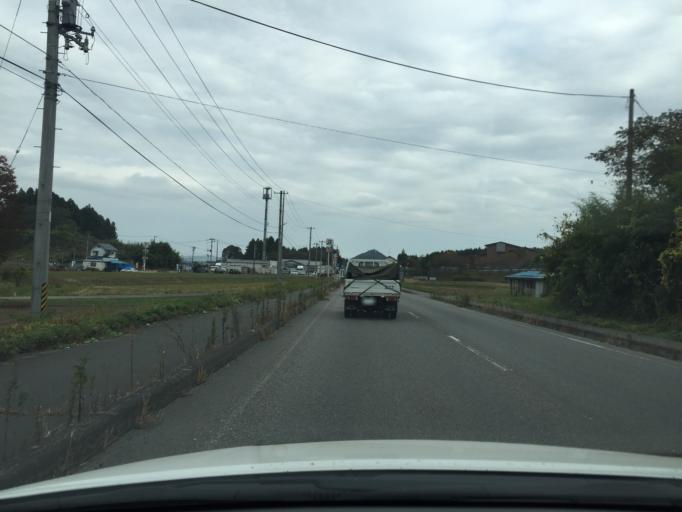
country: JP
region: Fukushima
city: Ishikawa
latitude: 37.0553
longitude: 140.3006
